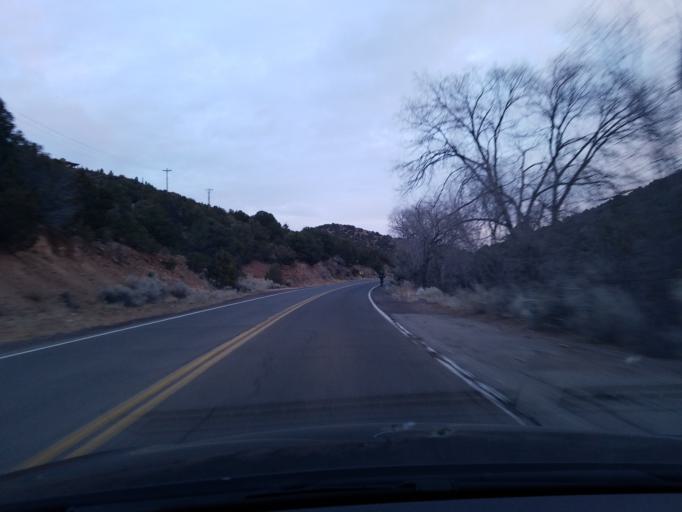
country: US
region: New Mexico
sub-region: Santa Fe County
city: Santa Fe
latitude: 35.7006
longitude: -105.9074
